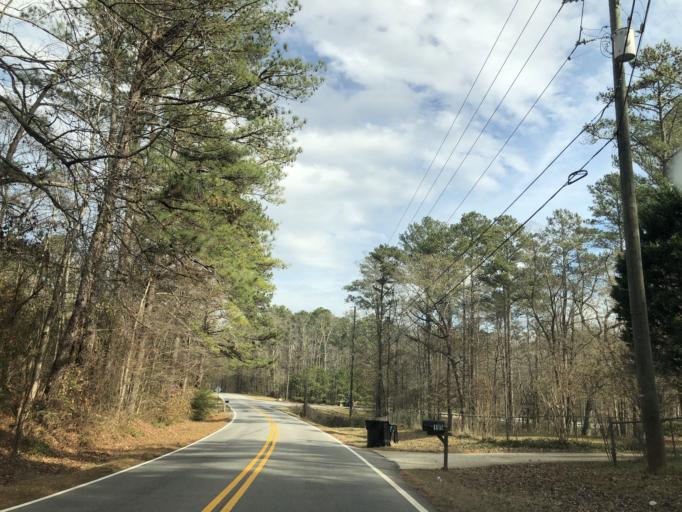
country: US
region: Georgia
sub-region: DeKalb County
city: Pine Mountain
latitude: 33.6428
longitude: -84.1932
